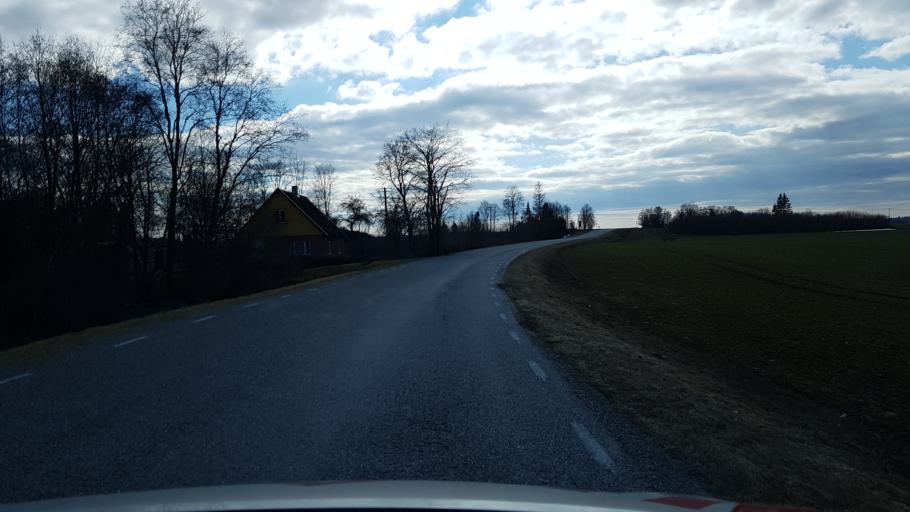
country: EE
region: Laeaene-Virumaa
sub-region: Kadrina vald
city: Kadrina
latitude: 59.2963
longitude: 26.2129
